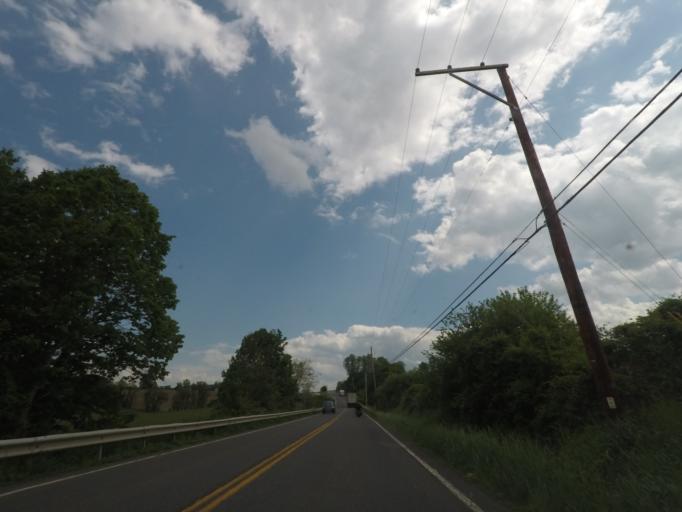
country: US
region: New York
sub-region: Dutchess County
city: Pine Plains
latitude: 42.0390
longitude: -73.6159
